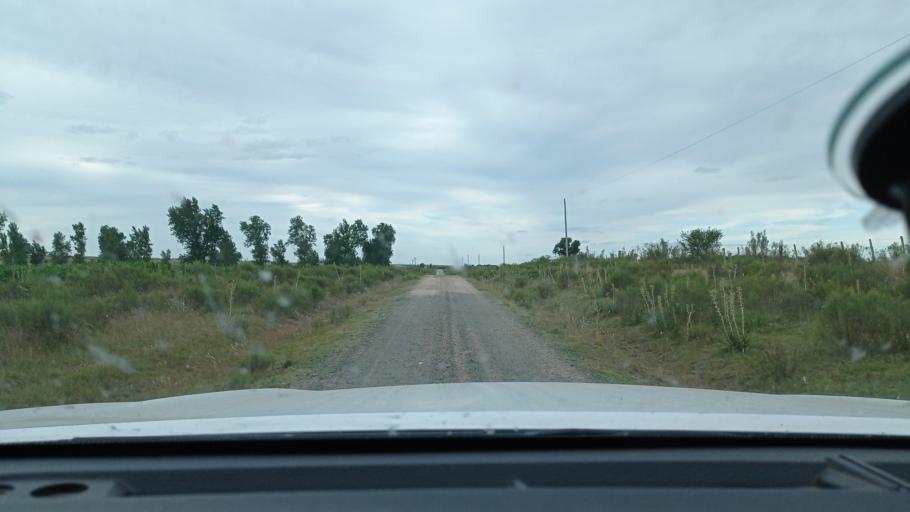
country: UY
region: Florida
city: Casupa
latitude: -34.1289
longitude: -55.7769
